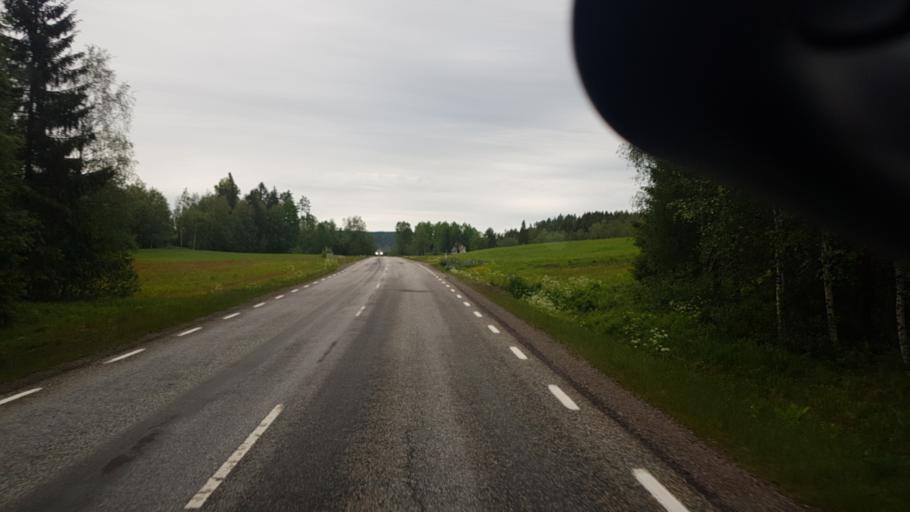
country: SE
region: Vaermland
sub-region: Arjangs Kommun
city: Arjaeng
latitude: 59.5689
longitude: 12.1232
